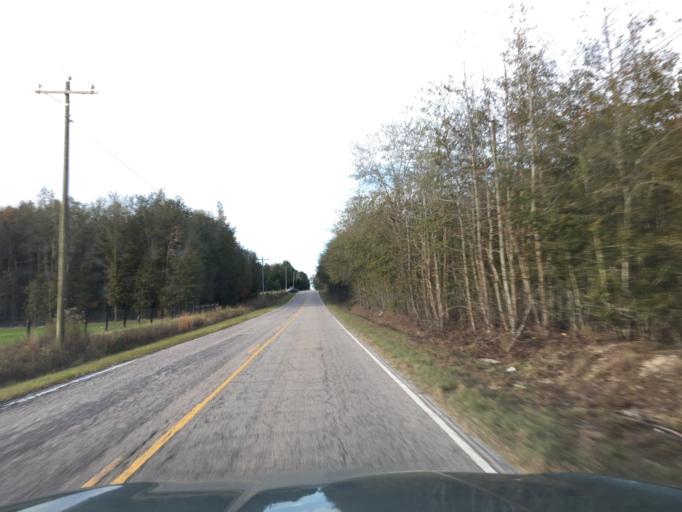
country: US
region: South Carolina
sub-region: Lexington County
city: Red Bank
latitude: 33.7376
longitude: -81.3617
